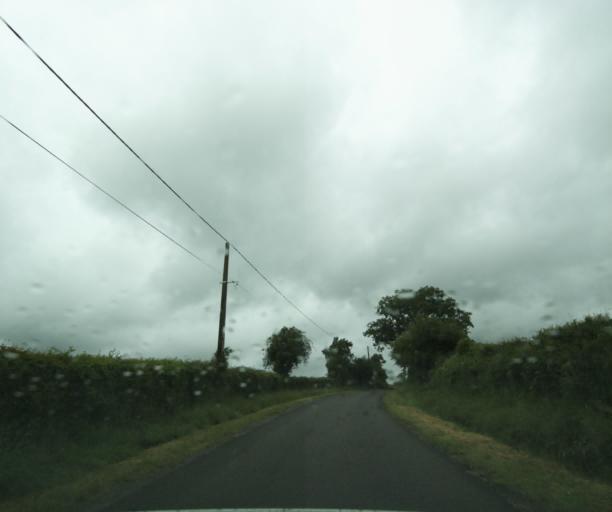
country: FR
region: Bourgogne
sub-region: Departement de Saone-et-Loire
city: Charolles
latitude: 46.4541
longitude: 4.4308
